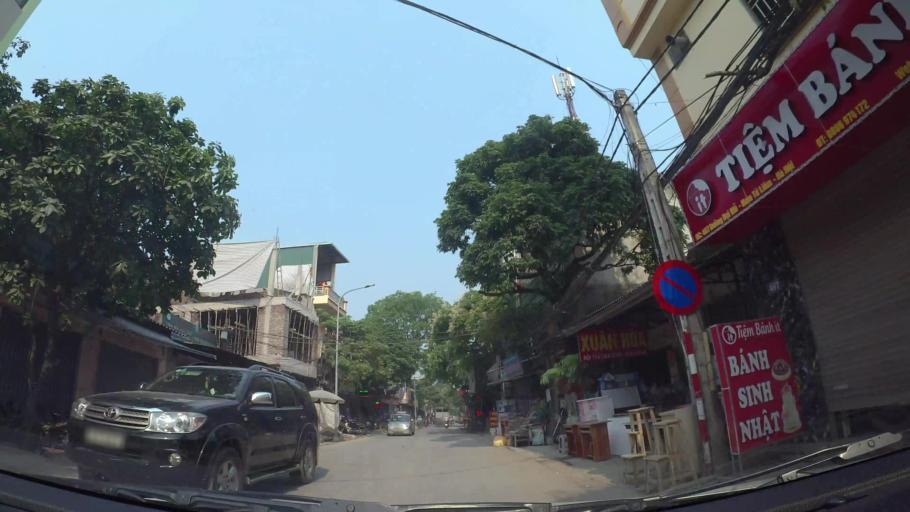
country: VN
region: Ha Noi
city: Ha Dong
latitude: 20.9957
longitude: 105.7533
